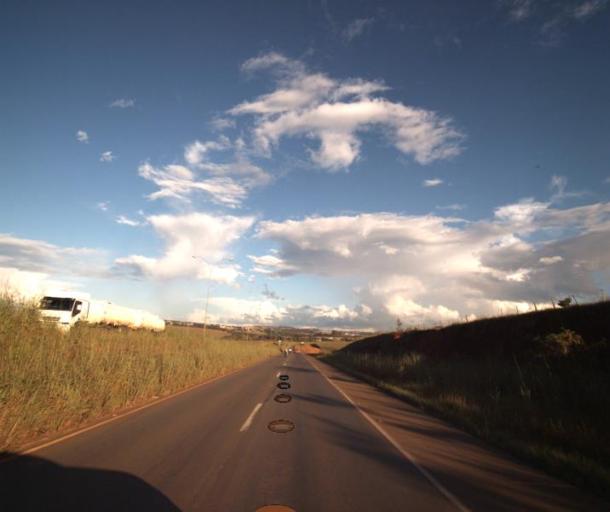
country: BR
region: Goias
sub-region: Anapolis
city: Anapolis
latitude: -16.2972
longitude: -48.9297
